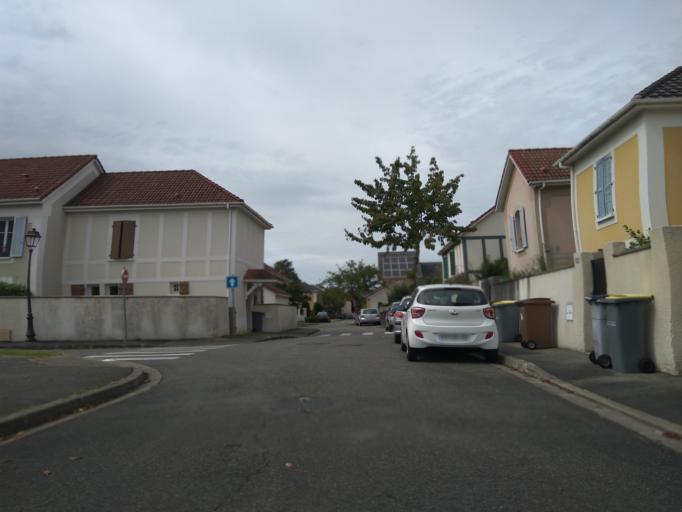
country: FR
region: Aquitaine
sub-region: Departement des Pyrenees-Atlantiques
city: Bizanos
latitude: 43.2990
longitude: -0.3391
